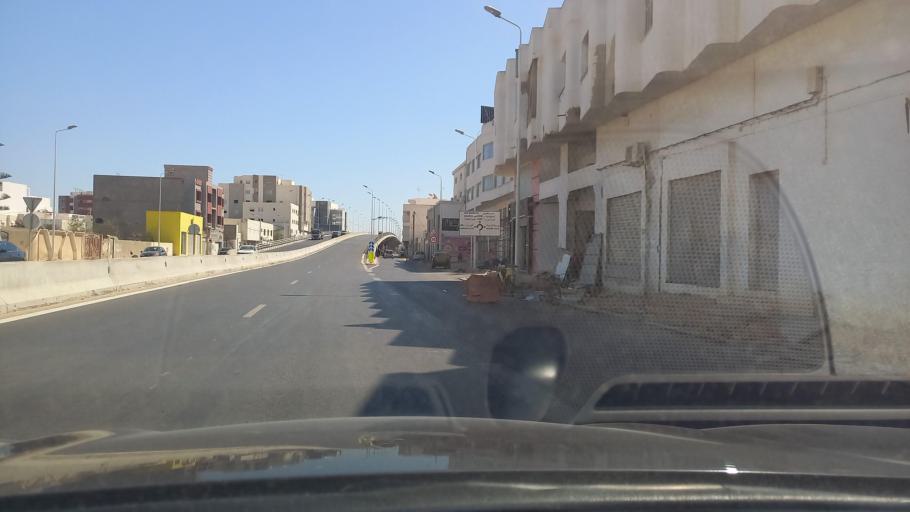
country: TN
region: Safaqis
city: Sfax
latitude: 34.7603
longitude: 10.7380
